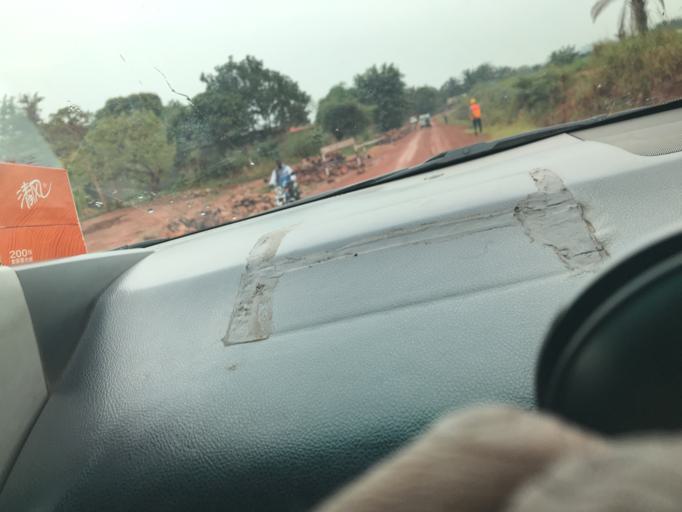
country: CD
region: Equateur
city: Gemena
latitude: 3.2349
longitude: 19.7799
